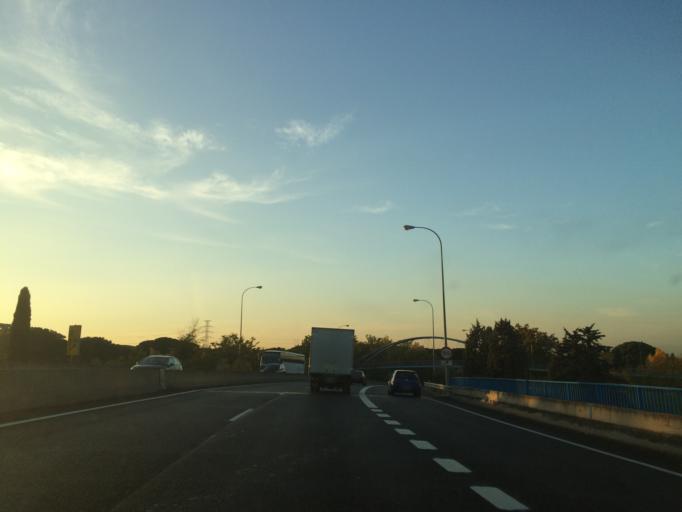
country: ES
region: Madrid
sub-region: Provincia de Madrid
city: Moncloa-Aravaca
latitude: 40.4347
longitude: -3.7382
